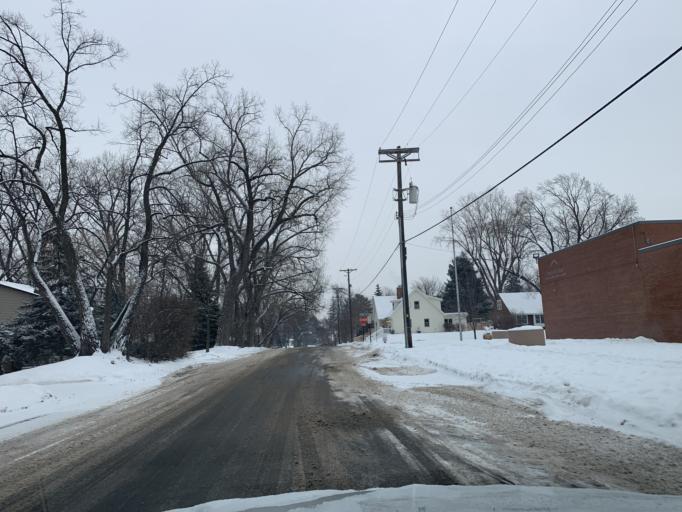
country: US
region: Minnesota
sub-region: Hennepin County
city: Saint Louis Park
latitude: 44.9521
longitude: -93.3347
